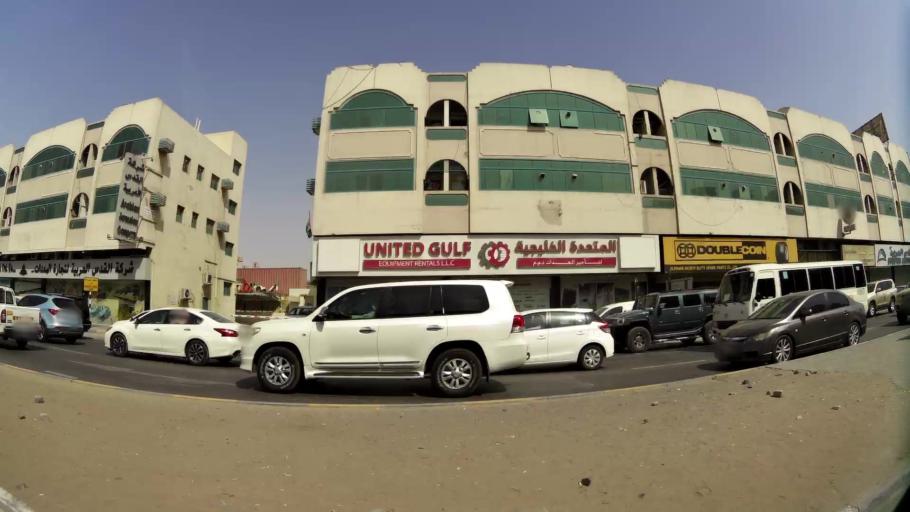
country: AE
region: Ash Shariqah
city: Sharjah
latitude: 25.3081
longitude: 55.4199
